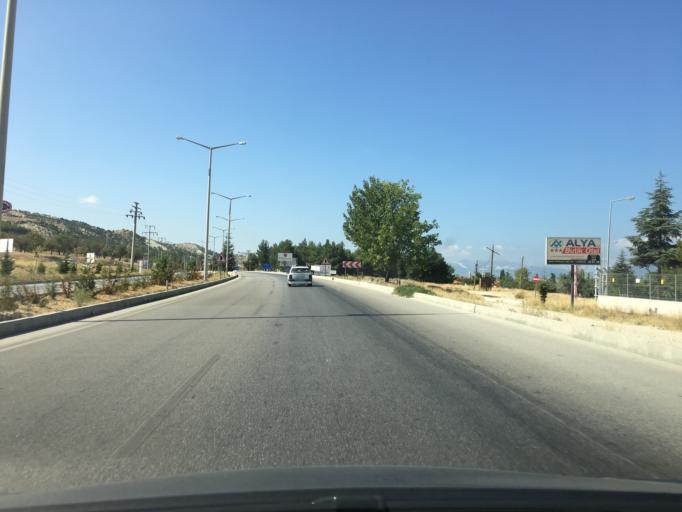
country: TR
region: Burdur
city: Burdur
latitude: 37.7553
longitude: 30.3366
